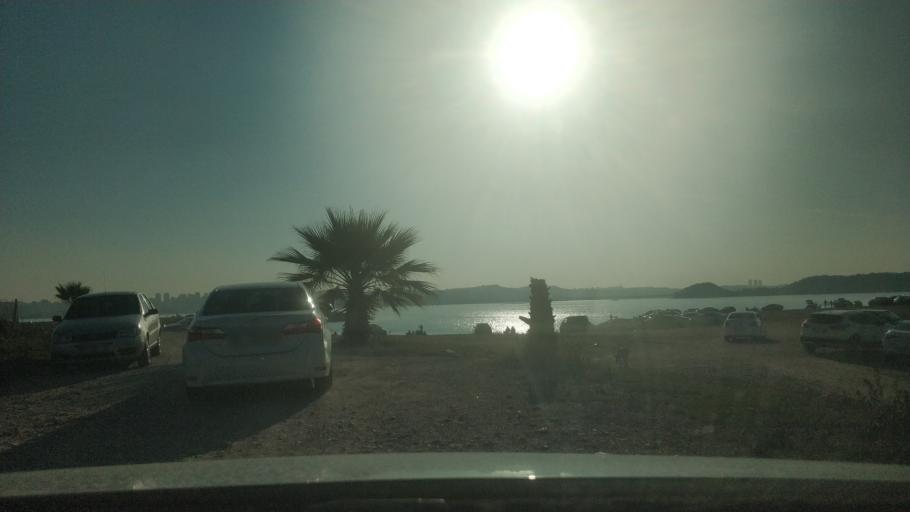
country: TR
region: Adana
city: Adana
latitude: 37.0951
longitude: 35.3000
